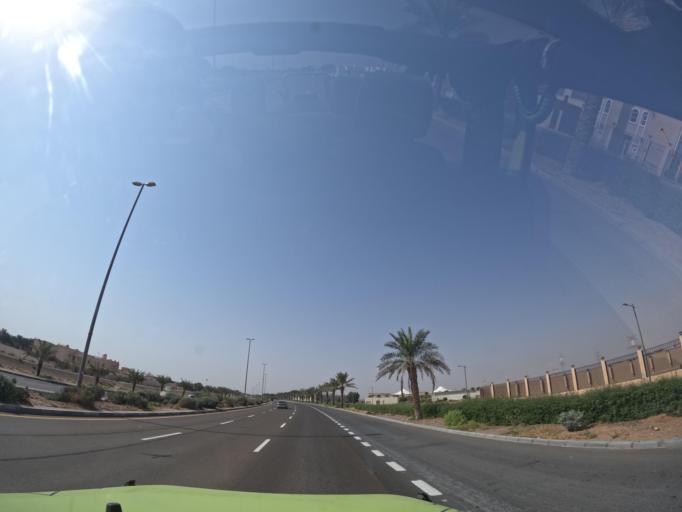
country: AE
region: Abu Dhabi
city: Al Ain
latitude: 24.2626
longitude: 55.6953
